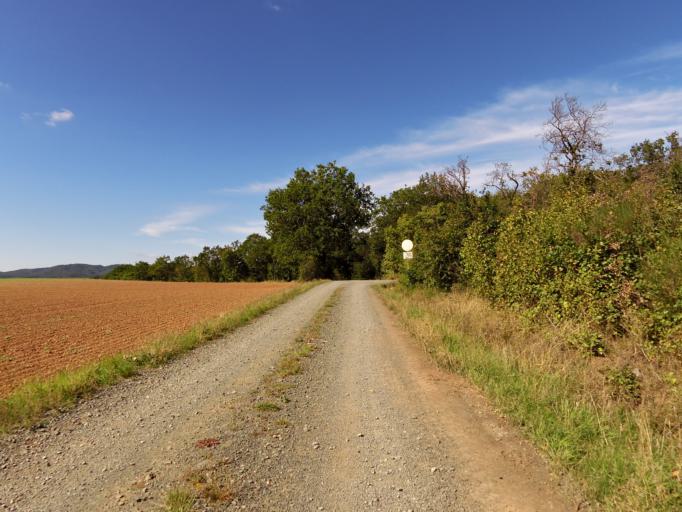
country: DE
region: Rheinland-Pfalz
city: Standenbuhl
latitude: 49.5797
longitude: 7.9852
